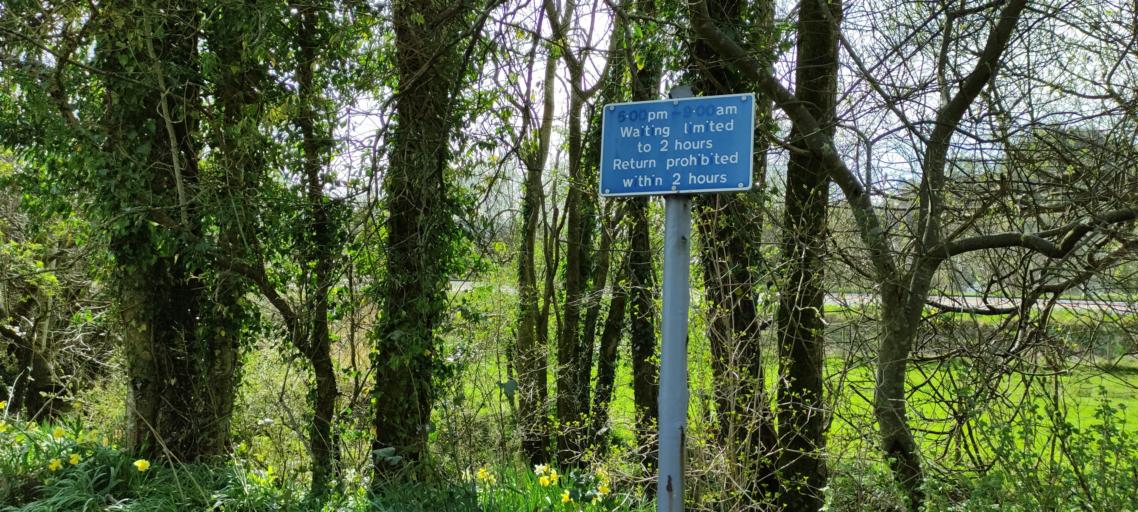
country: GB
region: England
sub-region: Cumbria
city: Keswick
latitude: 54.6018
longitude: -3.1703
